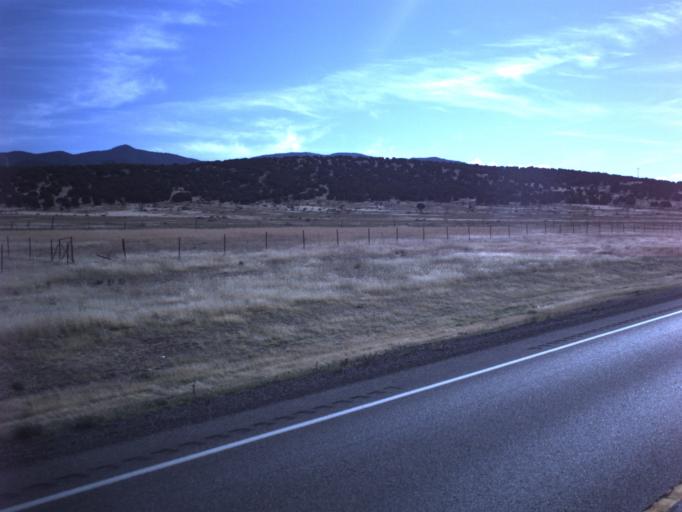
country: US
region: Utah
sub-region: Sanpete County
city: Gunnison
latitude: 39.3333
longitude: -111.9164
